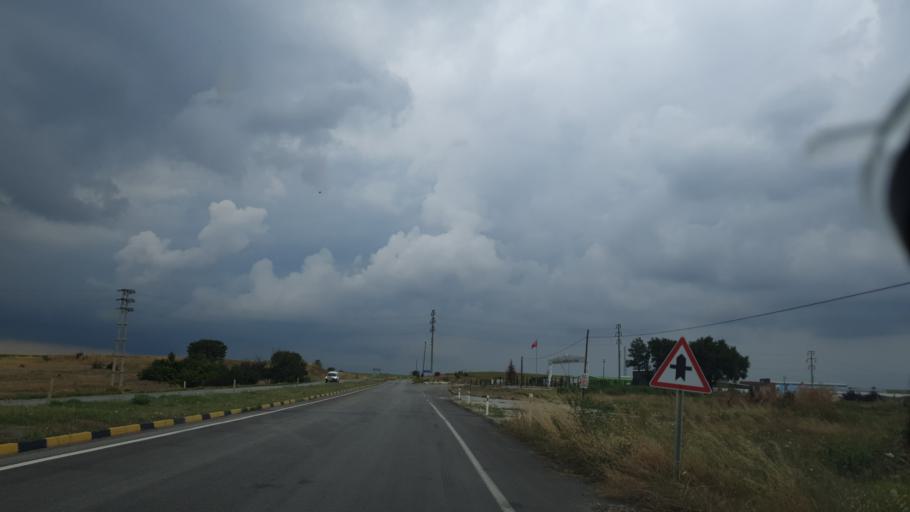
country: TR
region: Tekirdag
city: Hayrabolu
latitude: 41.2213
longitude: 27.0482
